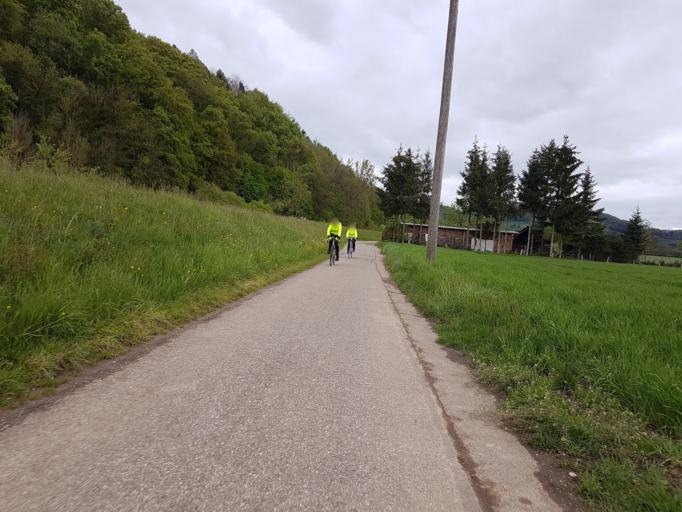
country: DE
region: Baden-Wuerttemberg
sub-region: Freiburg Region
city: Lauchringen
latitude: 47.6325
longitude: 8.3430
